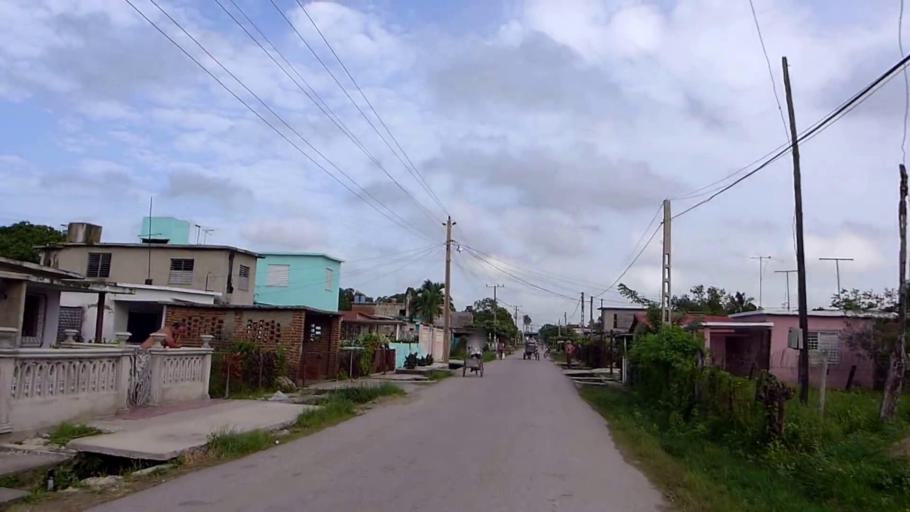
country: CU
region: Camaguey
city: Camaguey
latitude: 21.3819
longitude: -77.9416
